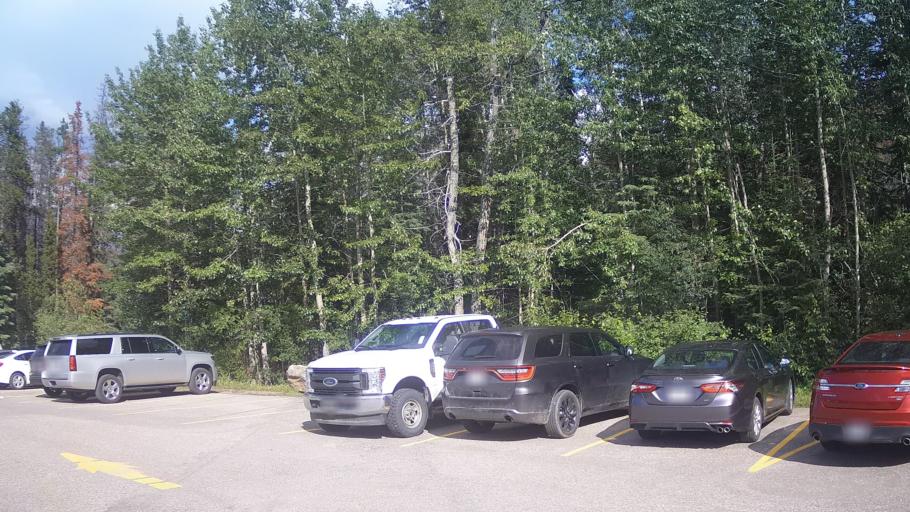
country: CA
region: Alberta
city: Jasper Park Lodge
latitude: 52.8505
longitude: -118.1235
